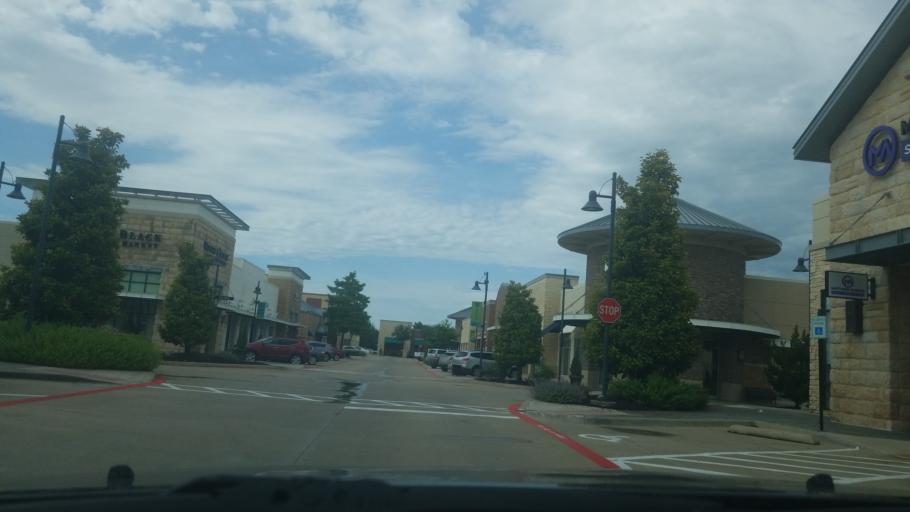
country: US
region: Texas
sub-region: Denton County
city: Copper Canyon
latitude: 33.0735
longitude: -97.0851
